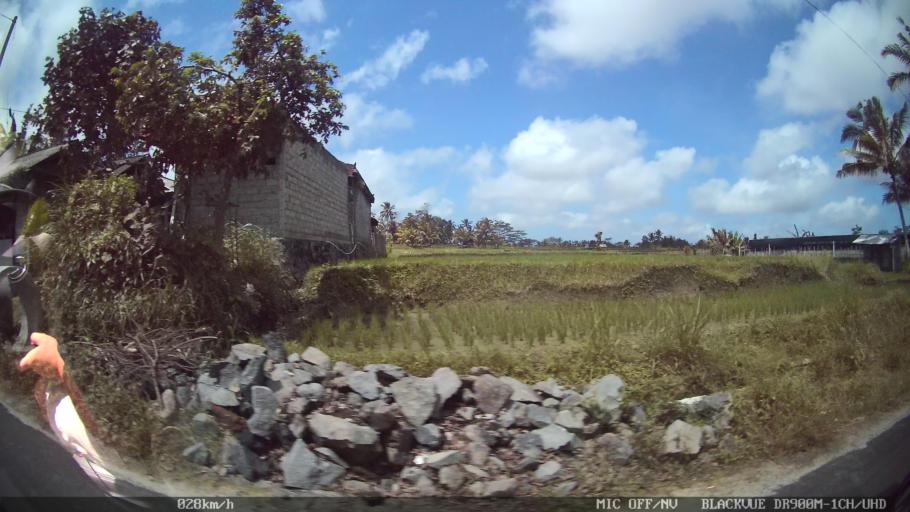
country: ID
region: Bali
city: Banjar Apuan Kaja
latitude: -8.4878
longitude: 115.3426
